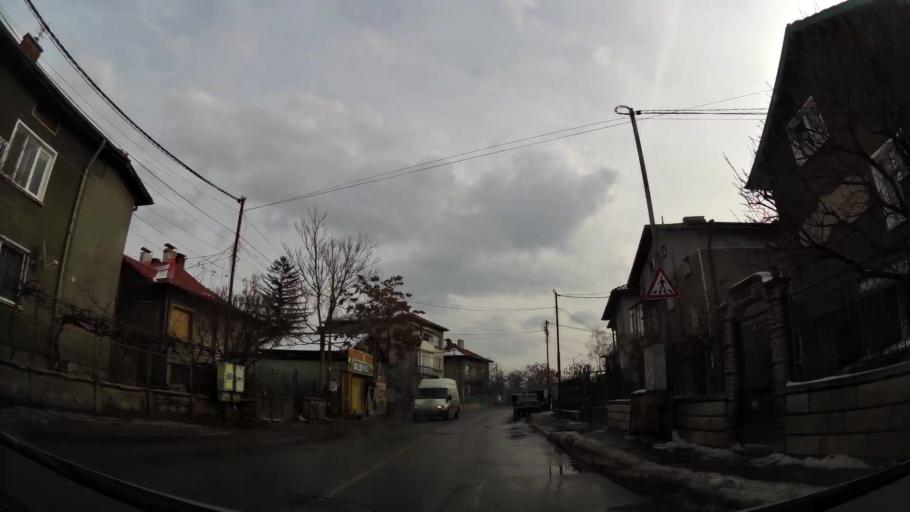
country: BG
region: Sofia-Capital
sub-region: Stolichna Obshtina
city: Sofia
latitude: 42.7051
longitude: 23.3858
